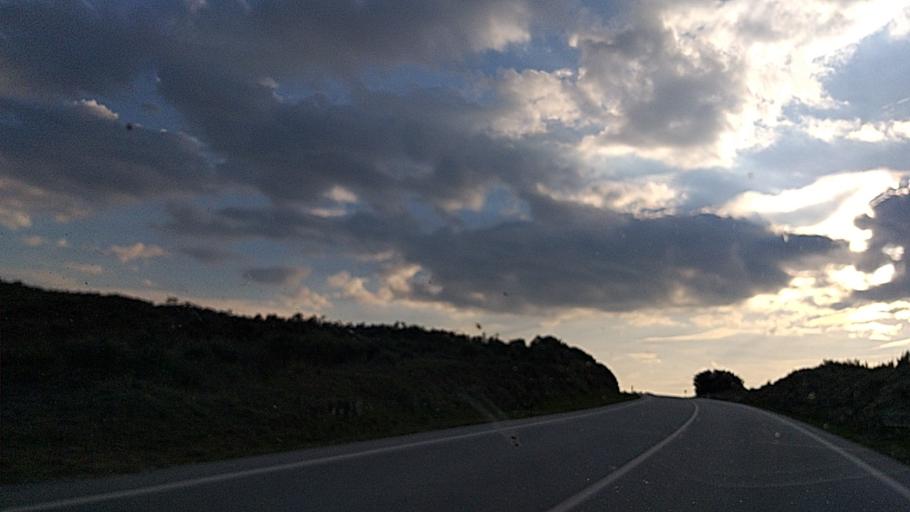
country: PT
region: Guarda
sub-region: Pinhel
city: Pinhel
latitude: 40.6861
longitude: -6.9475
